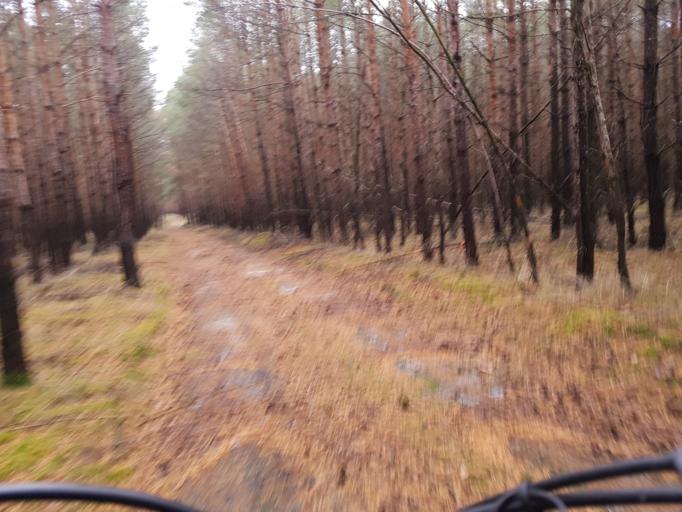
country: DE
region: Brandenburg
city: Schilda
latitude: 51.6200
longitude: 13.3835
